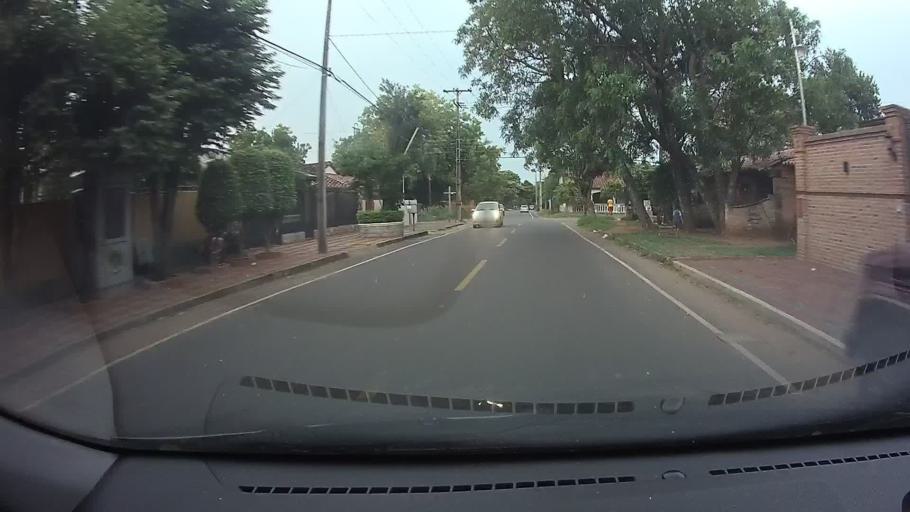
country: PY
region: Central
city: San Lorenzo
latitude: -25.2587
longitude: -57.5032
